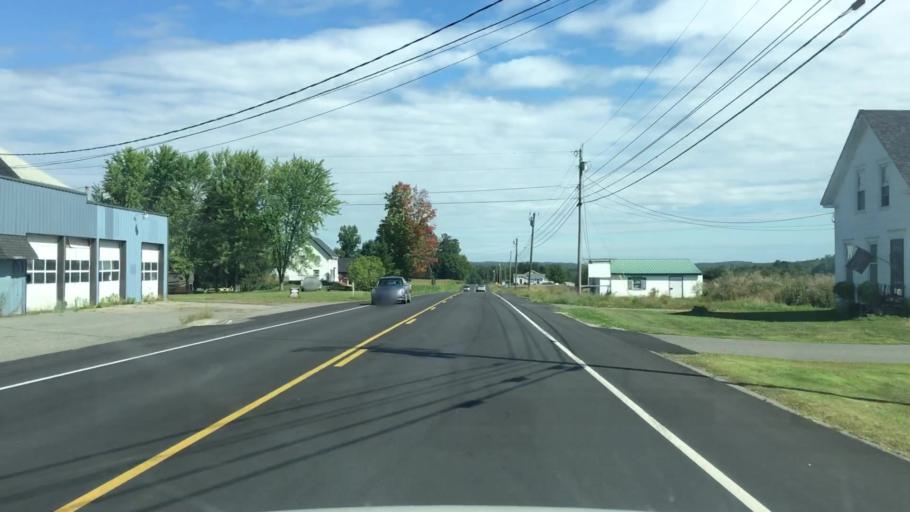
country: US
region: Maine
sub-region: Penobscot County
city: Corinna
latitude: 44.9324
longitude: -69.2522
